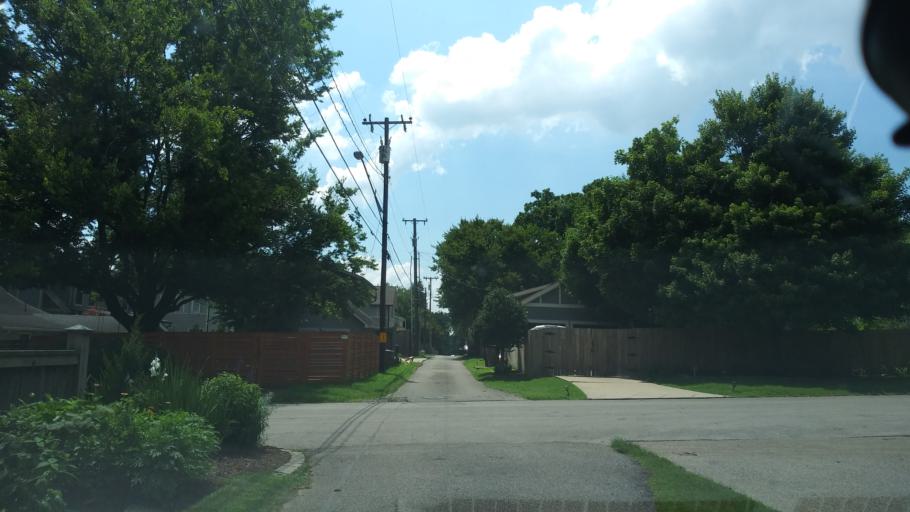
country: US
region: Tennessee
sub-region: Davidson County
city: Belle Meade
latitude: 36.1482
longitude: -86.8405
